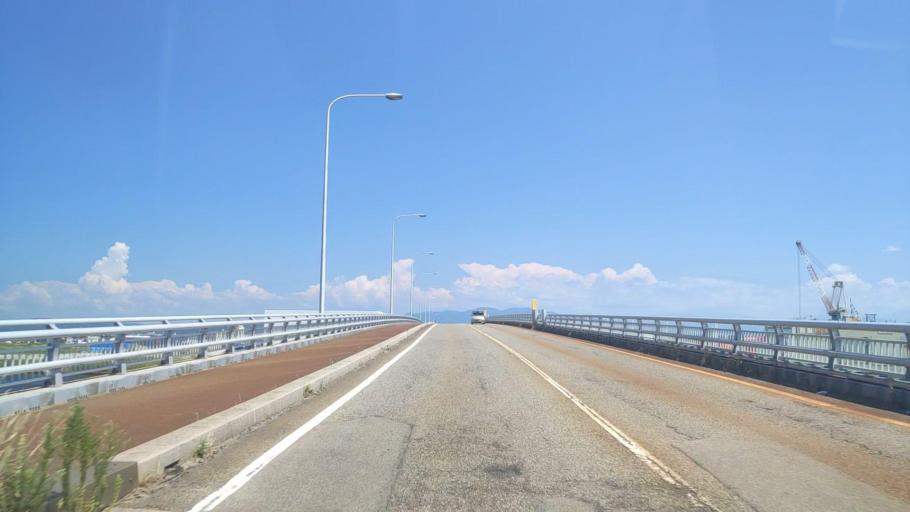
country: JP
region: Ishikawa
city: Kanazawa-shi
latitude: 36.6164
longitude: 136.6233
